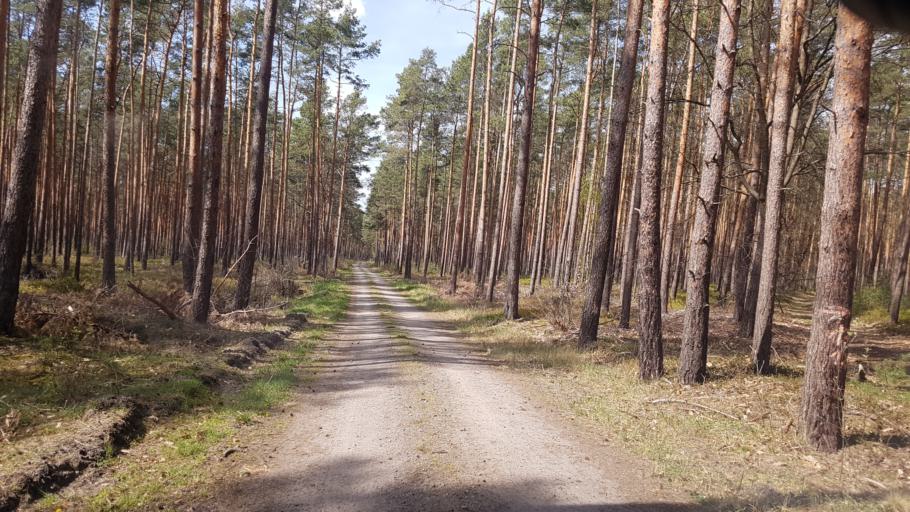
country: DE
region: Brandenburg
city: Plessa
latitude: 51.5459
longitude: 13.6575
